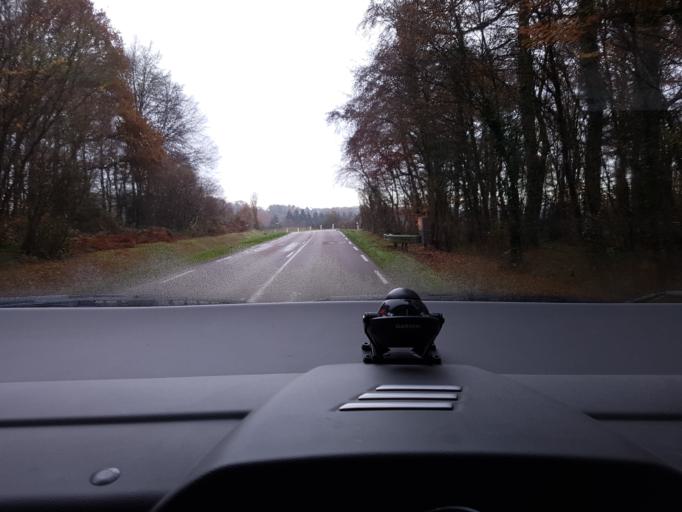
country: FR
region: Lower Normandy
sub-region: Departement de l'Orne
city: Saint-Sulpice-sur-Risle
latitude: 48.7851
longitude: 0.6639
